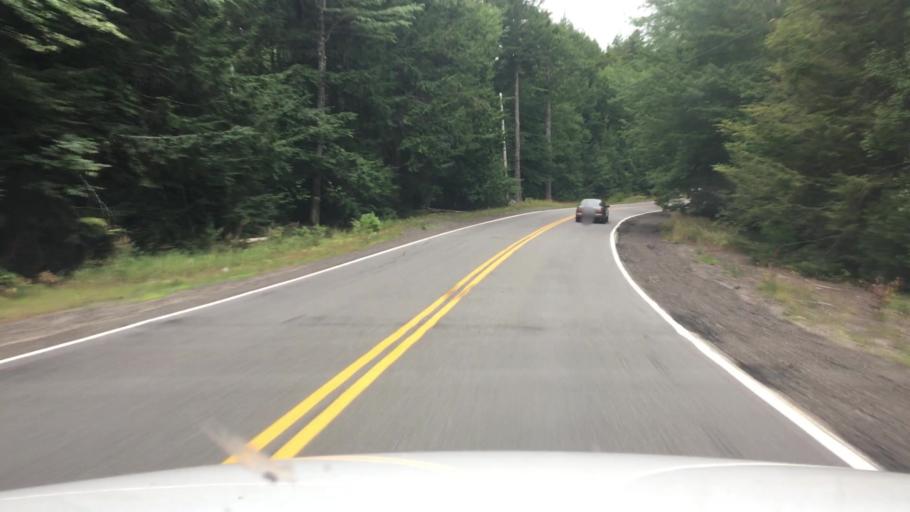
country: US
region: Maine
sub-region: Washington County
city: Cherryfield
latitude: 44.6052
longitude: -68.0415
